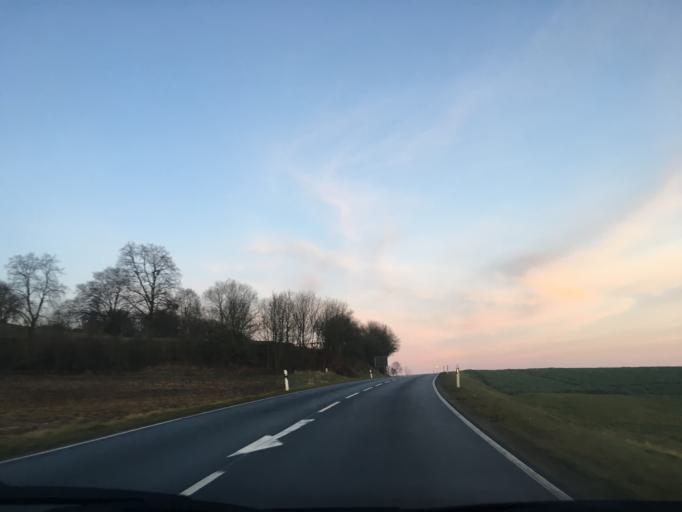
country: DE
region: Hesse
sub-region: Regierungsbezirk Kassel
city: Hofbieber
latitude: 50.5870
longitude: 9.8547
